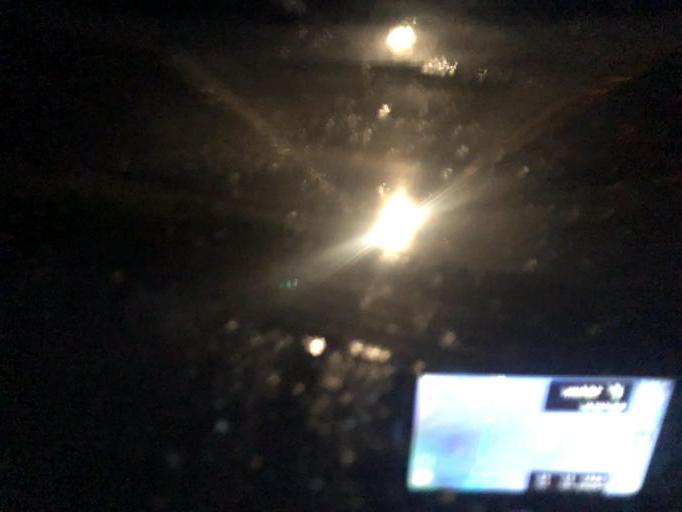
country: BR
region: Santa Catarina
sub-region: Guaramirim
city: Guaramirim
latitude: -26.4528
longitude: -48.9041
